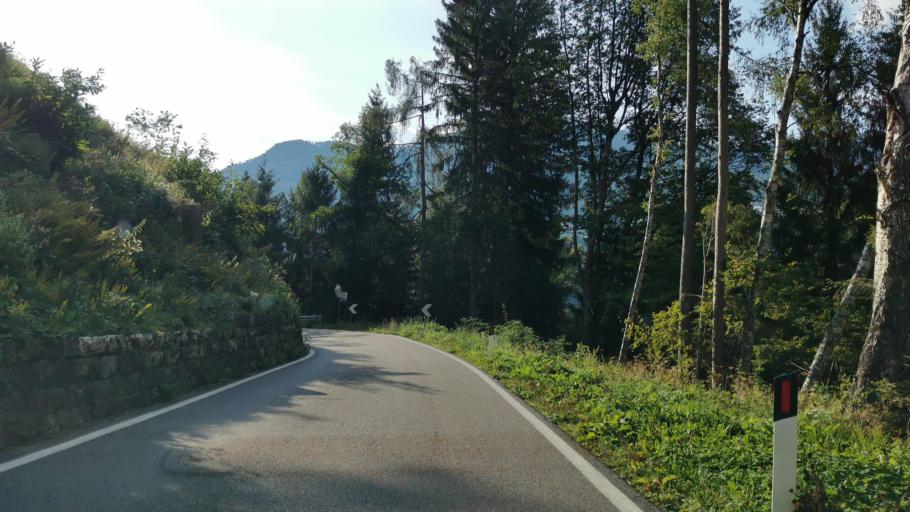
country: IT
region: Trentino-Alto Adige
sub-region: Provincia di Trento
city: Frassilongo
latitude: 46.0960
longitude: 11.3063
